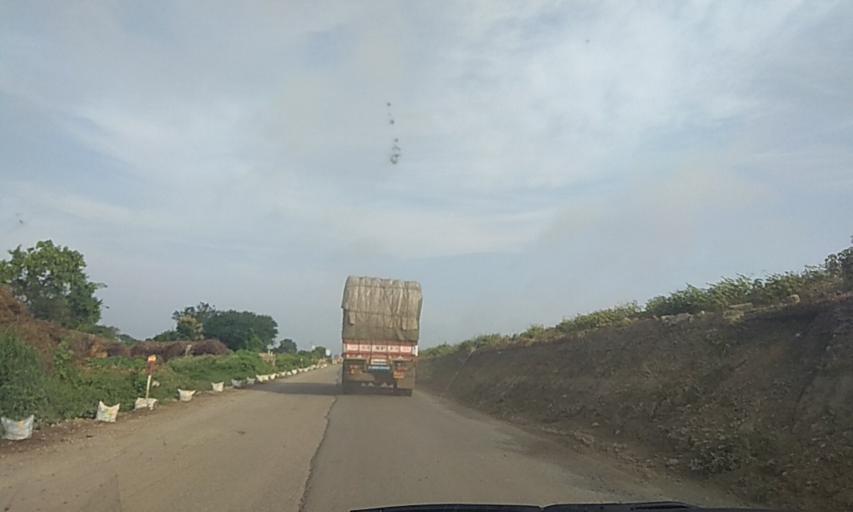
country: IN
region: Karnataka
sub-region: Haveri
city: Byadgi
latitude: 14.7204
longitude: 75.4801
